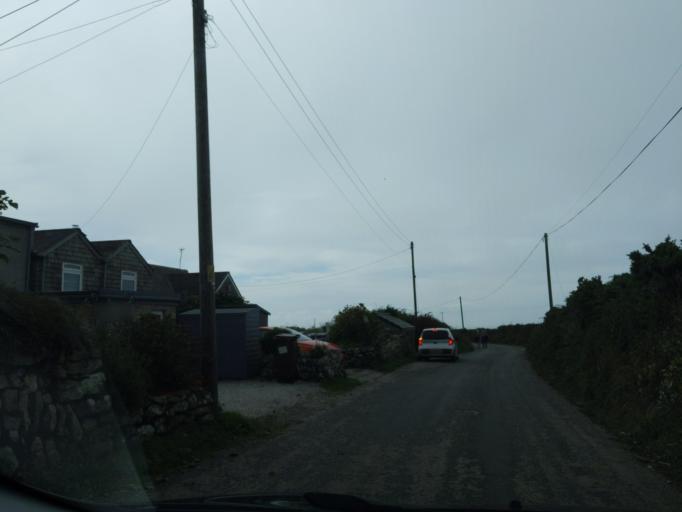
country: GB
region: England
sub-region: Cornwall
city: Germoe
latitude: 50.0997
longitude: -5.3626
